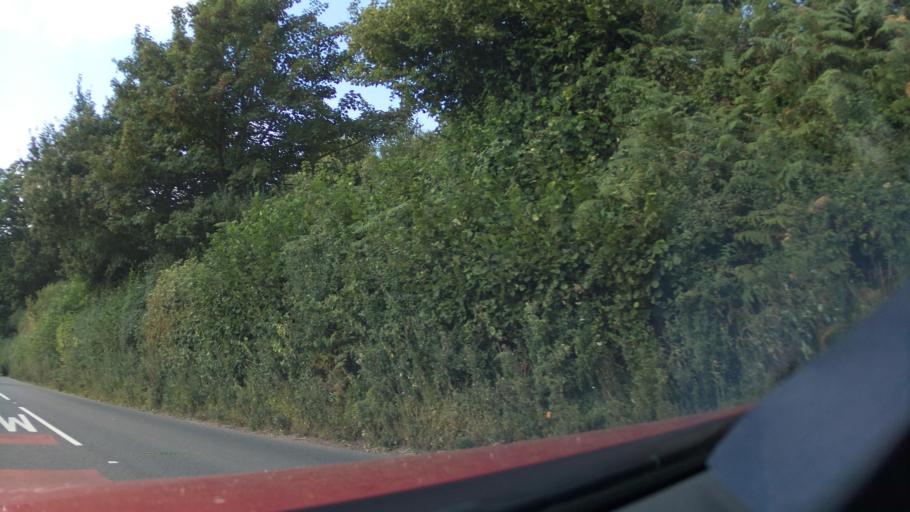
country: GB
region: England
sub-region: Devon
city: Tiverton
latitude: 50.8391
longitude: -3.5015
